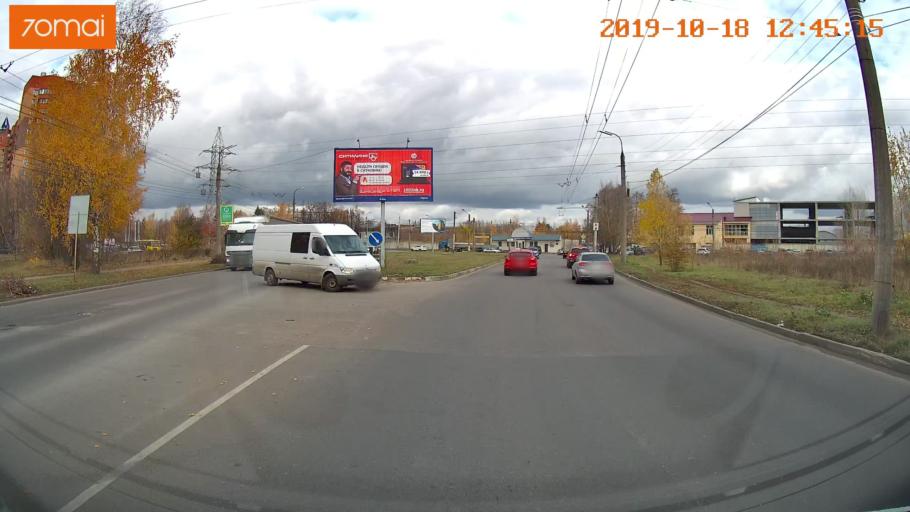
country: RU
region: Rjazan
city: Ryazan'
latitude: 54.6513
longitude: 39.6654
